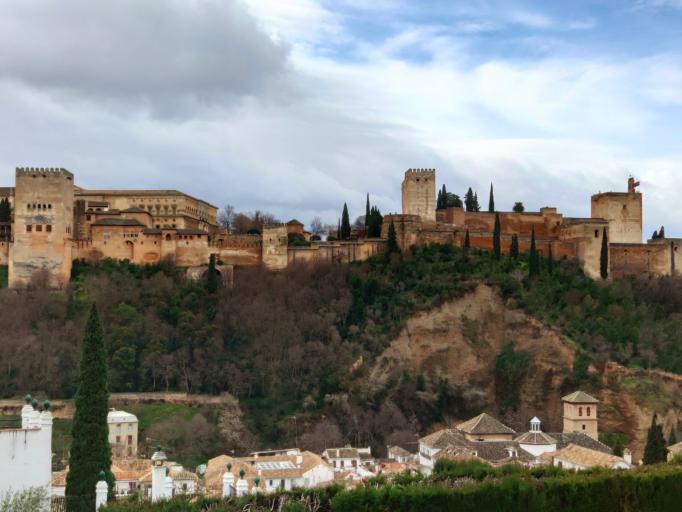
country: ES
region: Andalusia
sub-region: Provincia de Granada
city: Granada
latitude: 37.1811
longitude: -3.5906
